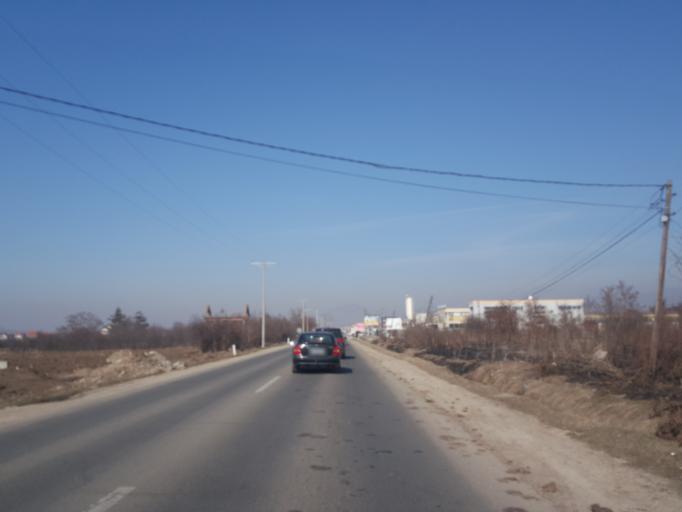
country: XK
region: Mitrovica
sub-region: Vushtrri
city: Vushtrri
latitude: 42.7973
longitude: 20.9984
